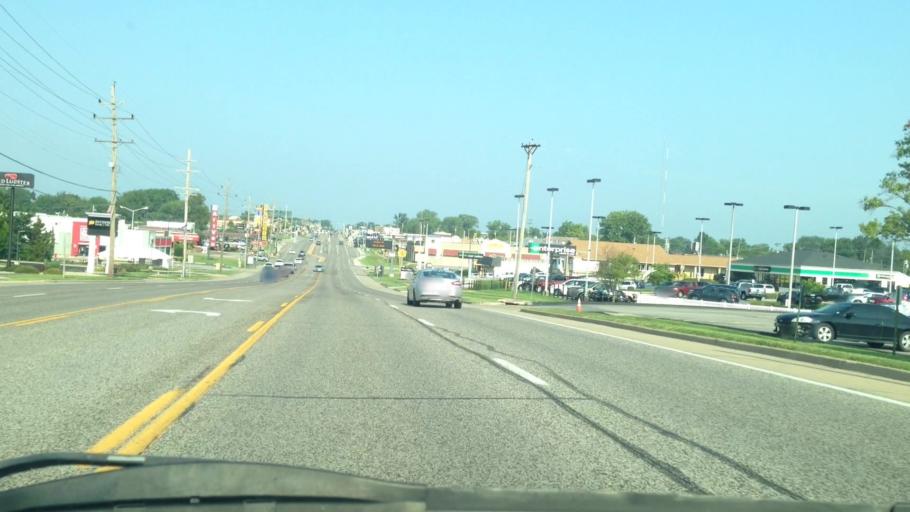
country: US
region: Missouri
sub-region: Saint Louis County
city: Concord
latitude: 38.5227
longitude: -90.3491
